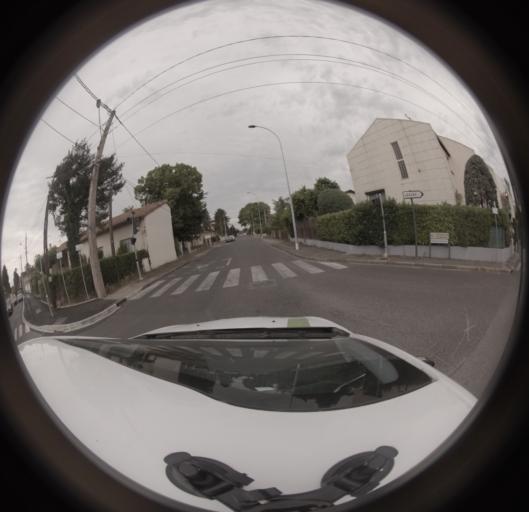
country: FR
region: Midi-Pyrenees
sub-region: Departement du Tarn-et-Garonne
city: Montauban
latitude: 44.0154
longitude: 1.3786
